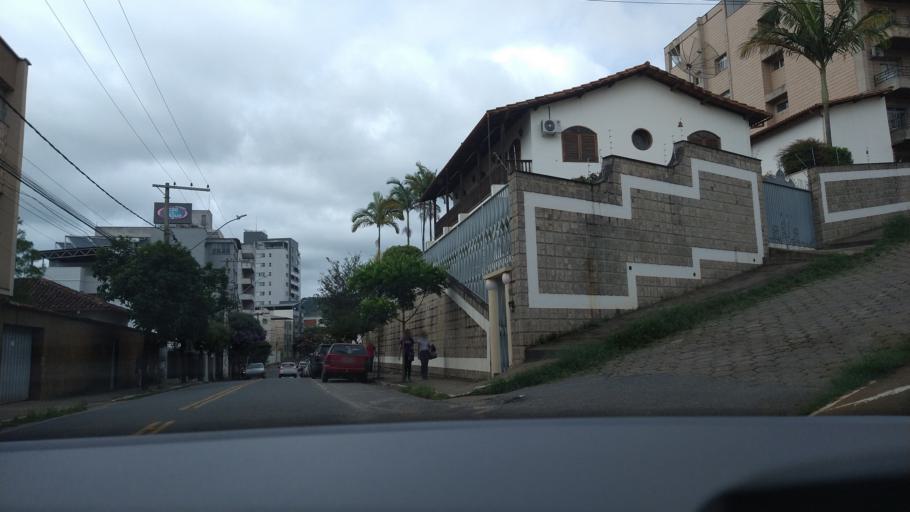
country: BR
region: Minas Gerais
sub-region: Vicosa
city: Vicosa
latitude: -20.7603
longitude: -42.8811
